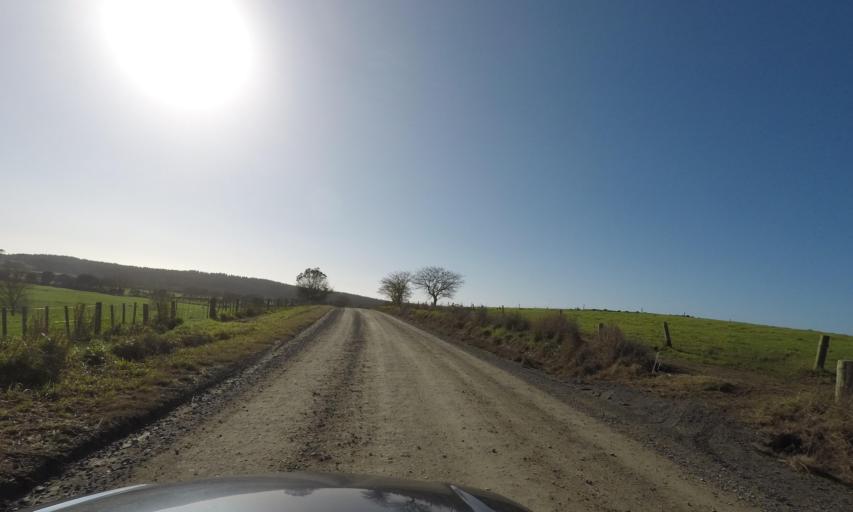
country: NZ
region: Auckland
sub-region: Auckland
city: Wellsford
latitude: -36.1605
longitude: 174.6098
